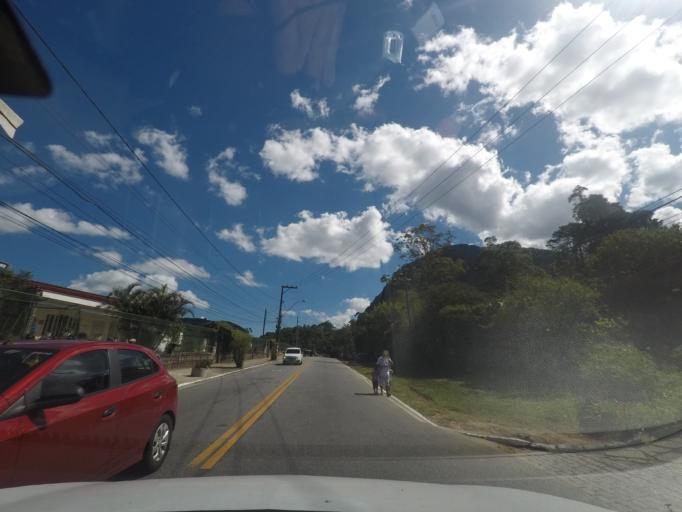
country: BR
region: Rio de Janeiro
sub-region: Teresopolis
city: Teresopolis
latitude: -22.4466
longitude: -42.9820
